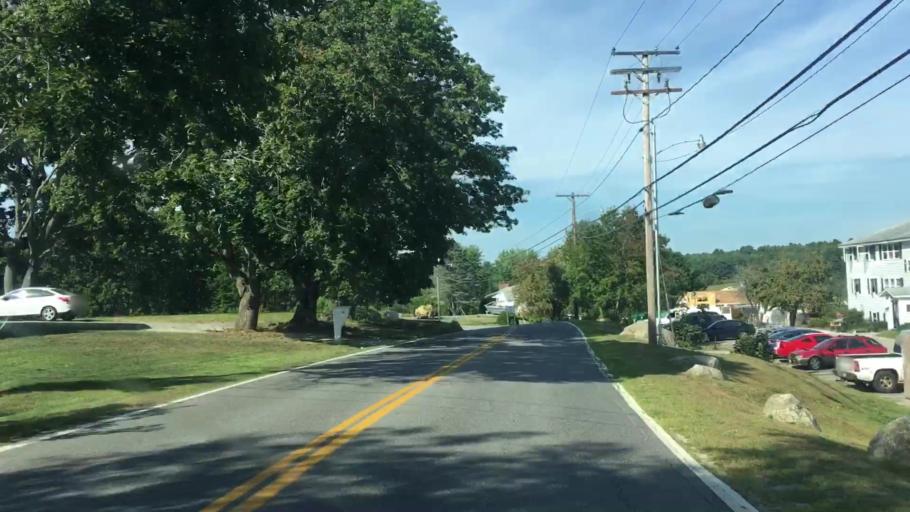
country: US
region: Maine
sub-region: Sagadahoc County
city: Bath
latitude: 43.9255
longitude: -69.8589
